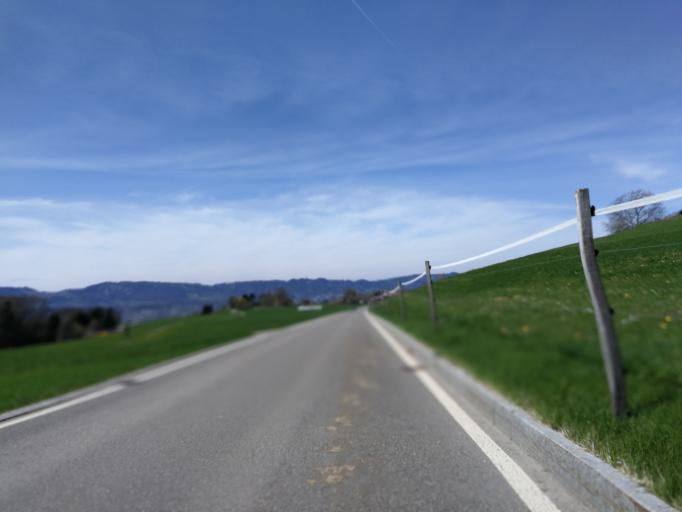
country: CH
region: Zurich
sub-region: Bezirk Meilen
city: Meilen
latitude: 47.2916
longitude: 8.6402
